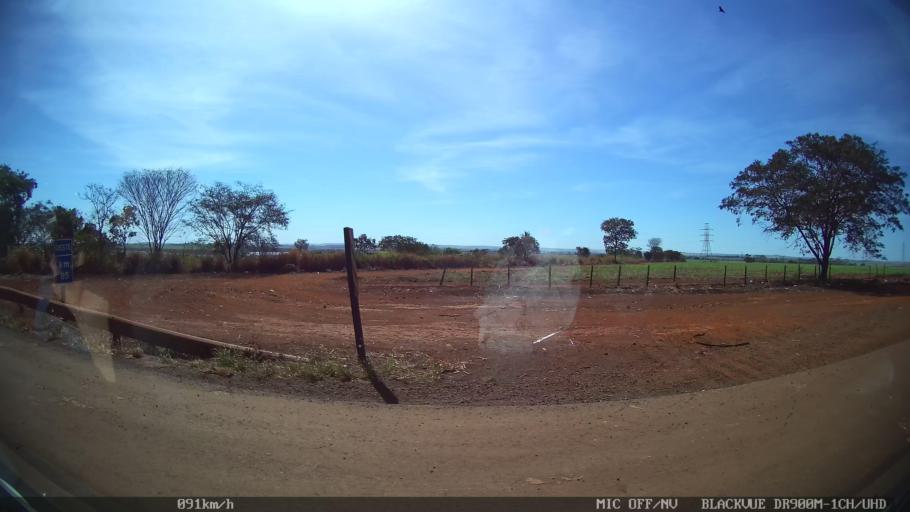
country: BR
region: Sao Paulo
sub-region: Sao Joaquim Da Barra
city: Sao Joaquim da Barra
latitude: -20.5223
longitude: -47.8564
